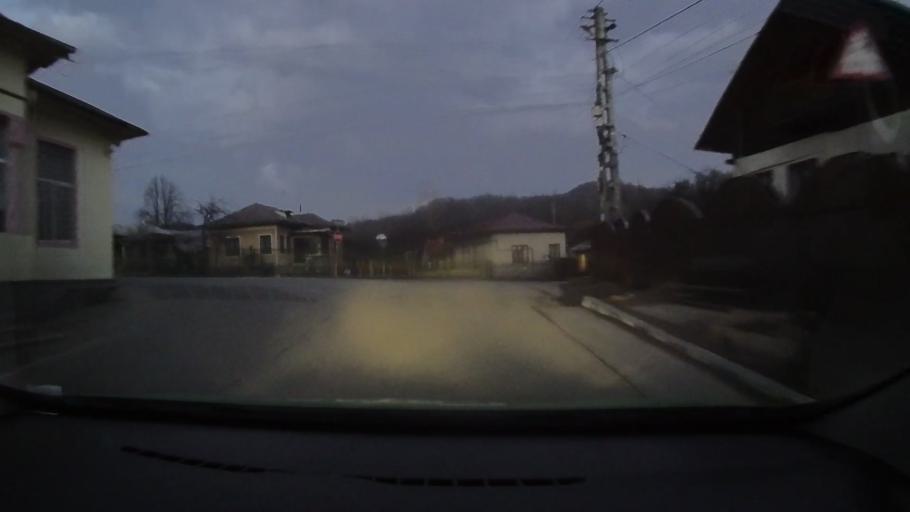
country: RO
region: Prahova
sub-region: Comuna Provita de Jos
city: Draganeasa
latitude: 45.1190
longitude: 25.6693
